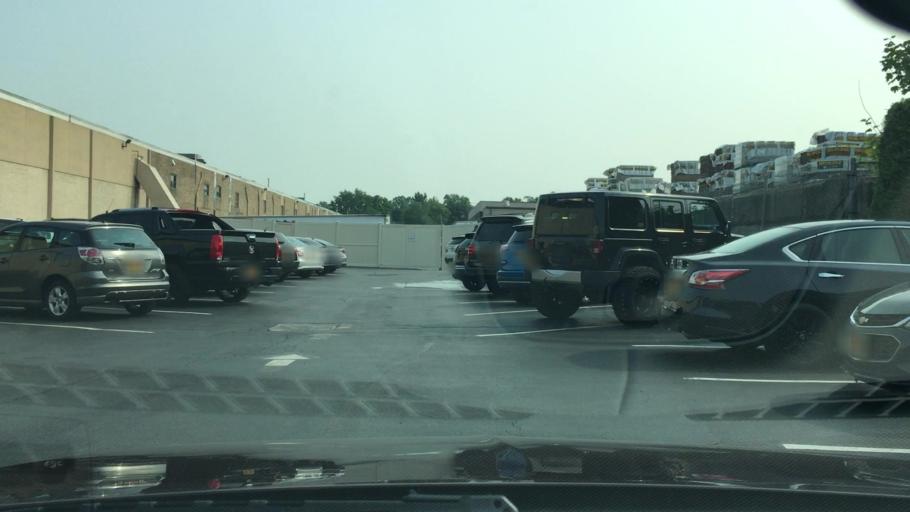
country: US
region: New York
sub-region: Nassau County
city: Westbury
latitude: 40.7563
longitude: -73.5790
